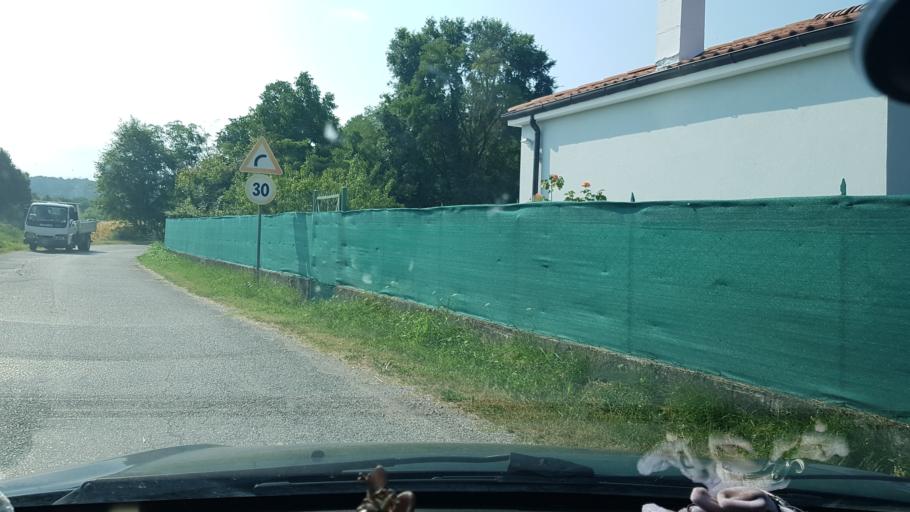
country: IT
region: Friuli Venezia Giulia
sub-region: Provincia di Gorizia
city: Fogliano
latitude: 45.8634
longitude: 13.4787
